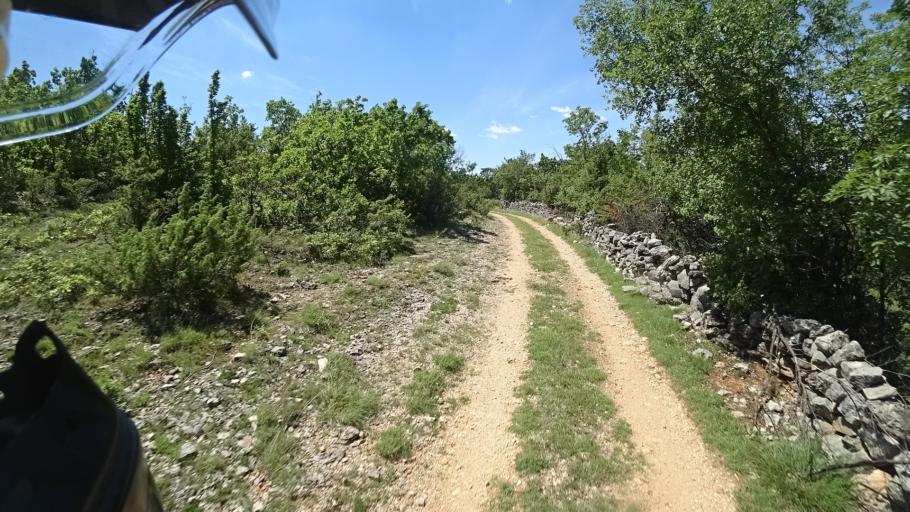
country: HR
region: Sibensko-Kniniska
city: Knin
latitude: 44.0232
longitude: 16.2649
